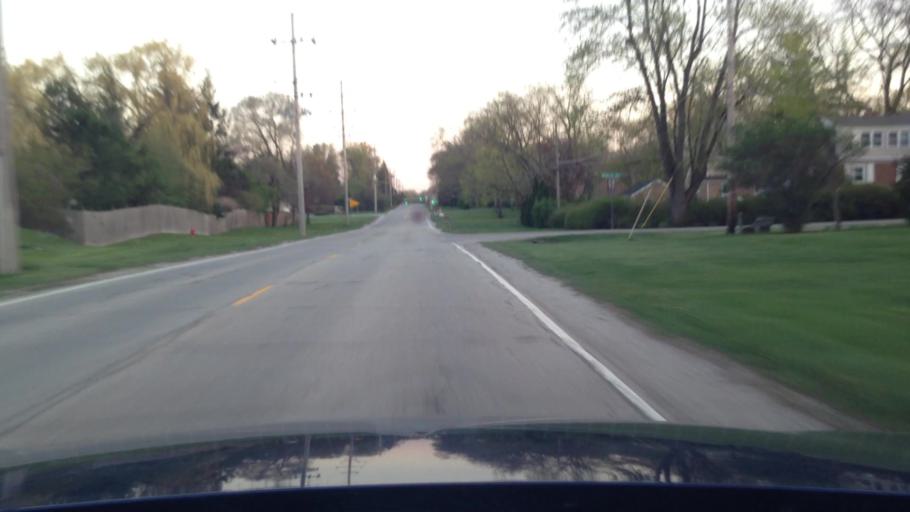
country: US
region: Illinois
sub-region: Cook County
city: Prospect Heights
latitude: 42.1012
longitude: -87.9272
